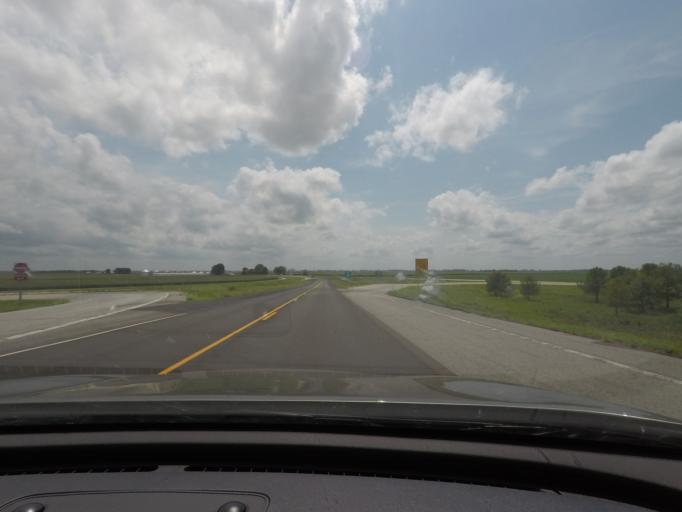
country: US
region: Missouri
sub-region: Carroll County
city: Carrollton
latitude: 39.3376
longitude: -93.4915
